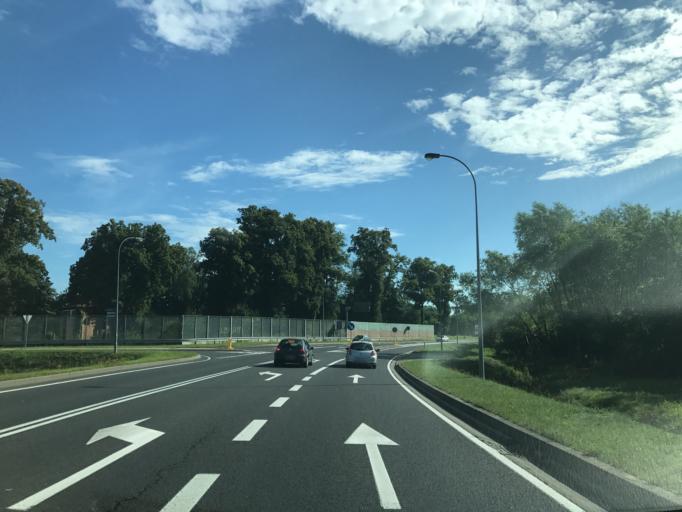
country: PL
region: West Pomeranian Voivodeship
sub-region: Powiat slawienski
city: Slawno
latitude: 54.3644
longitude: 16.7018
